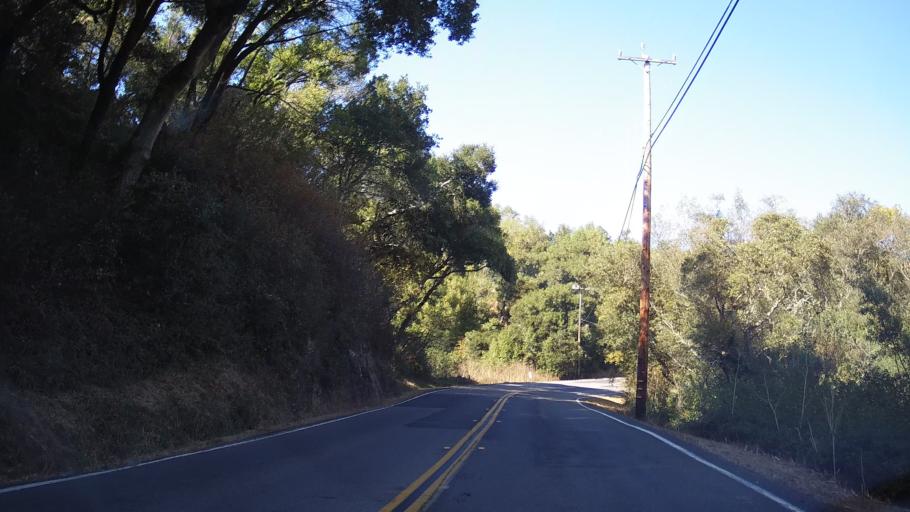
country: US
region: California
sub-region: Marin County
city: Inverness
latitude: 38.0805
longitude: -122.7849
